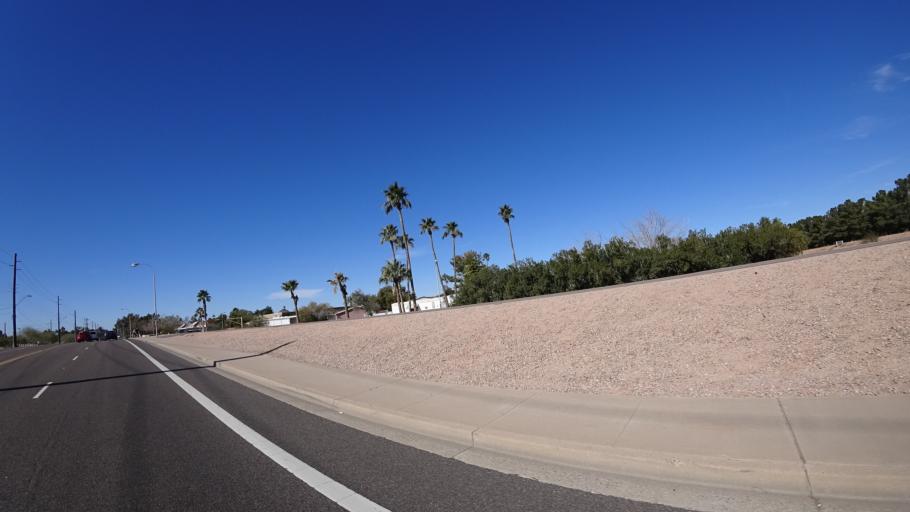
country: US
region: Arizona
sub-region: Maricopa County
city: Tempe
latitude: 33.4513
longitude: -111.9140
